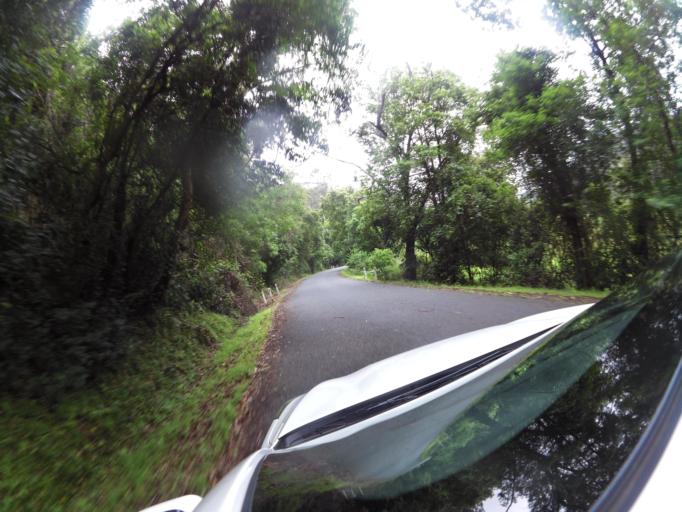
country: AU
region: New South Wales
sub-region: Hornsby Shire
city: Glenorie
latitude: -33.4283
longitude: 150.9588
